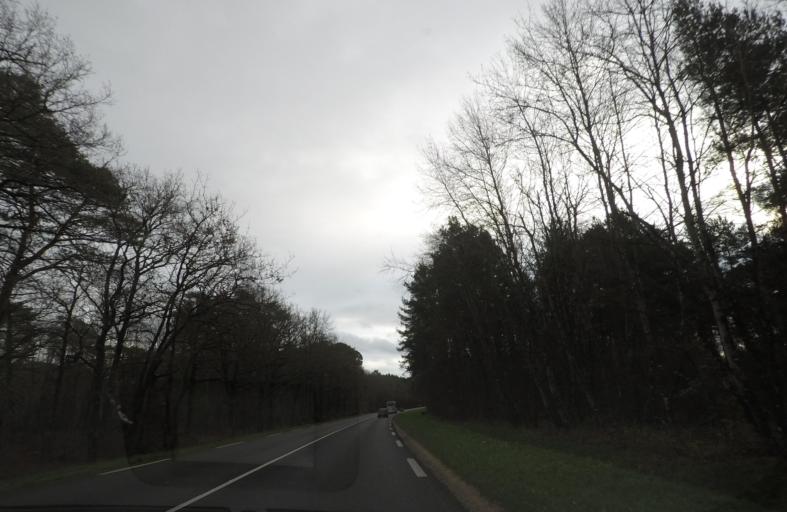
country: FR
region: Centre
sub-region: Departement du Loir-et-Cher
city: Mur-de-Sologne
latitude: 47.4048
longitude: 1.6268
